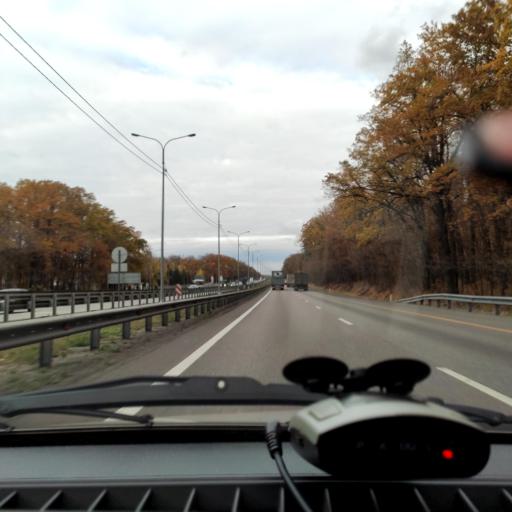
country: RU
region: Voronezj
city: Podgornoye
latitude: 51.8517
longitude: 39.2151
